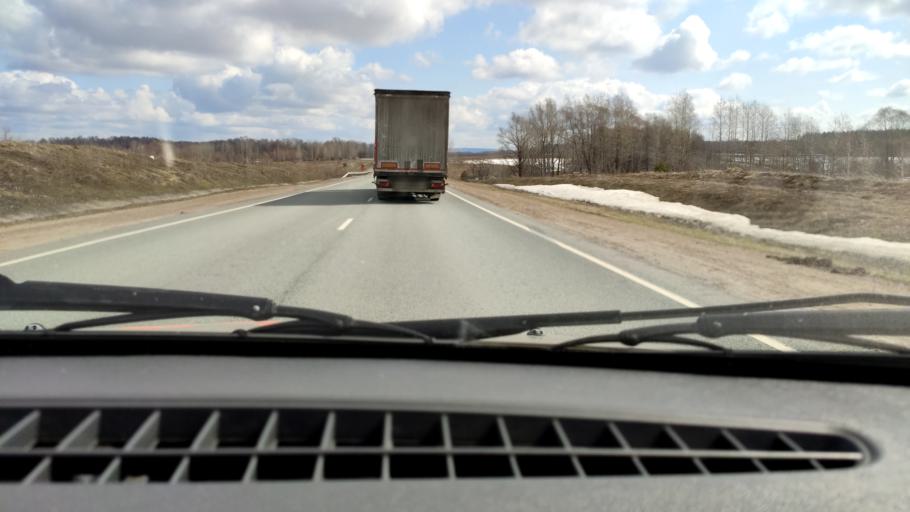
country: RU
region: Bashkortostan
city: Kudeyevskiy
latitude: 54.8171
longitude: 56.7849
